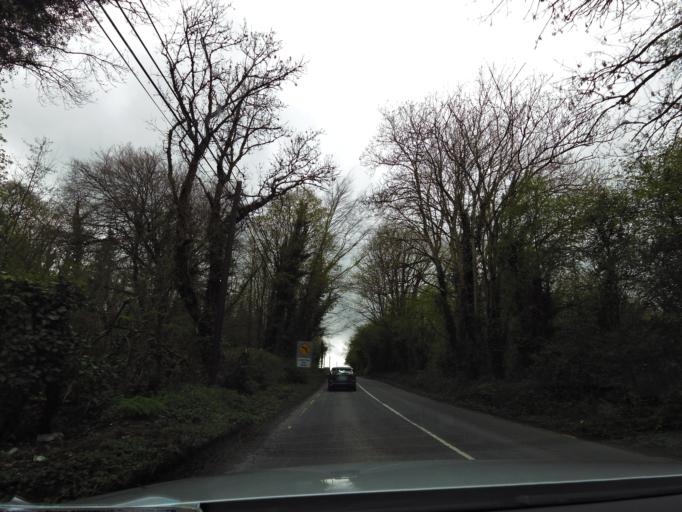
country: IE
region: Leinster
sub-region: Kilkenny
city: Ballyragget
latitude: 52.7317
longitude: -7.4499
